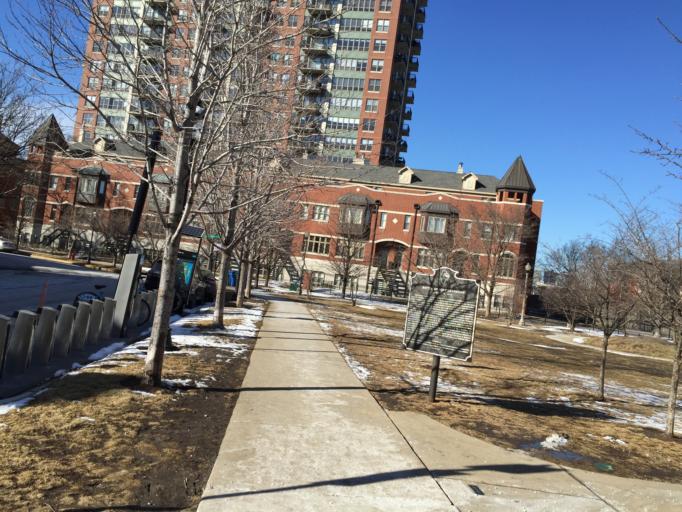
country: US
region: Illinois
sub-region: Cook County
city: Chicago
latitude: 41.8575
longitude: -87.6194
